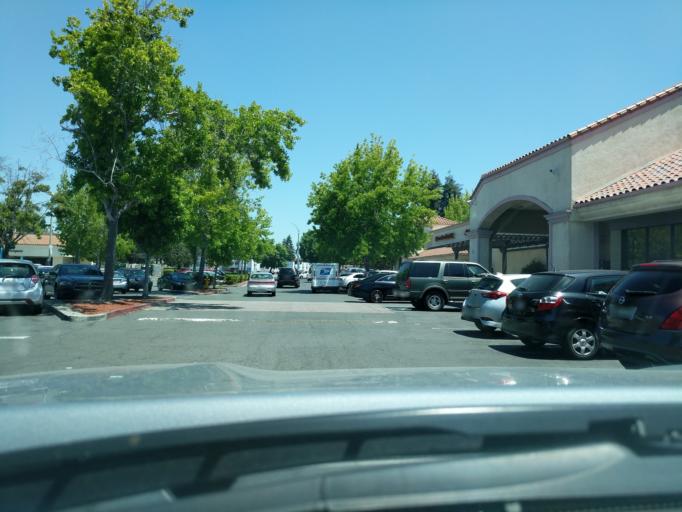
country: US
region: California
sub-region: Alameda County
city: Hayward
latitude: 37.6478
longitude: -122.0905
